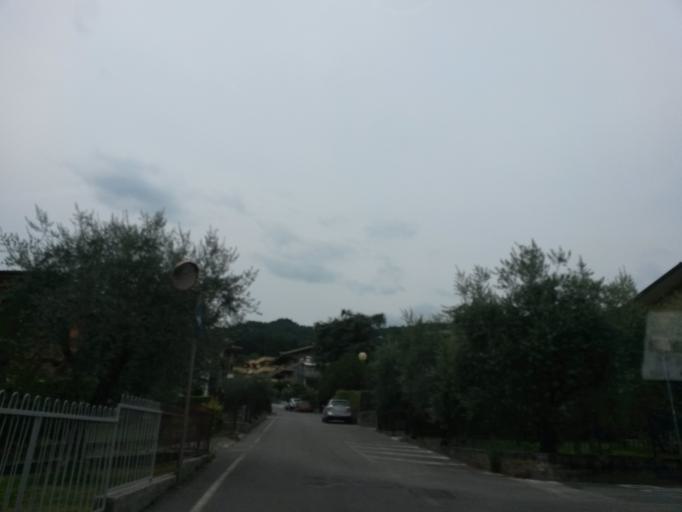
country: IT
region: Lombardy
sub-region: Provincia di Brescia
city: Salo
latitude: 45.6044
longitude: 10.5099
